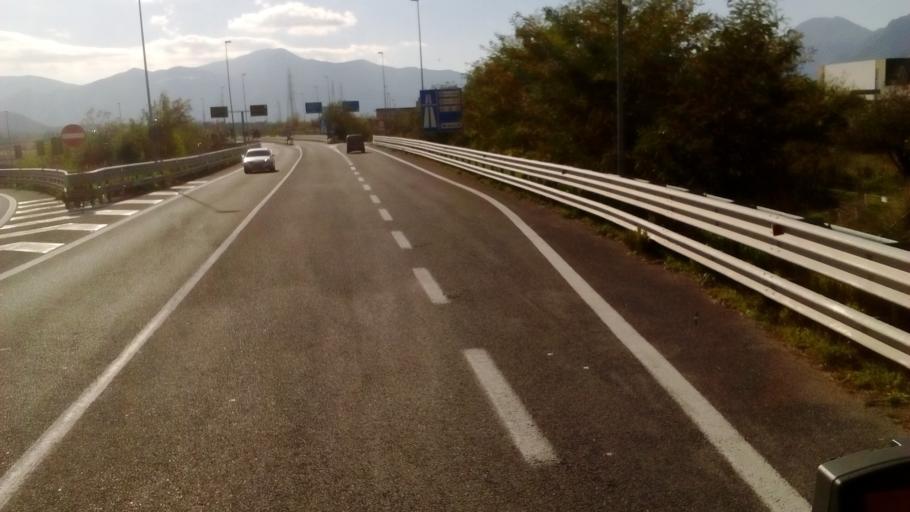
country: IT
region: Molise
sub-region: Provincia di Isernia
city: Taverna Ravindola
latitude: 41.5106
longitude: 14.1149
